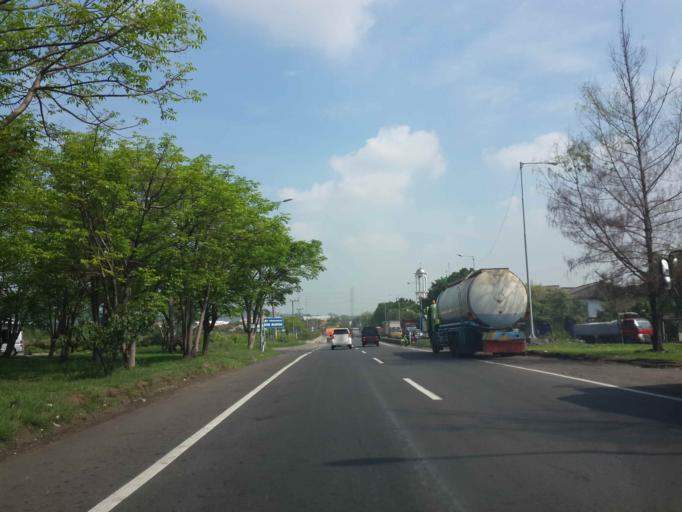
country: ID
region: East Java
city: Kebomas
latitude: -7.1996
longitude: 112.6458
